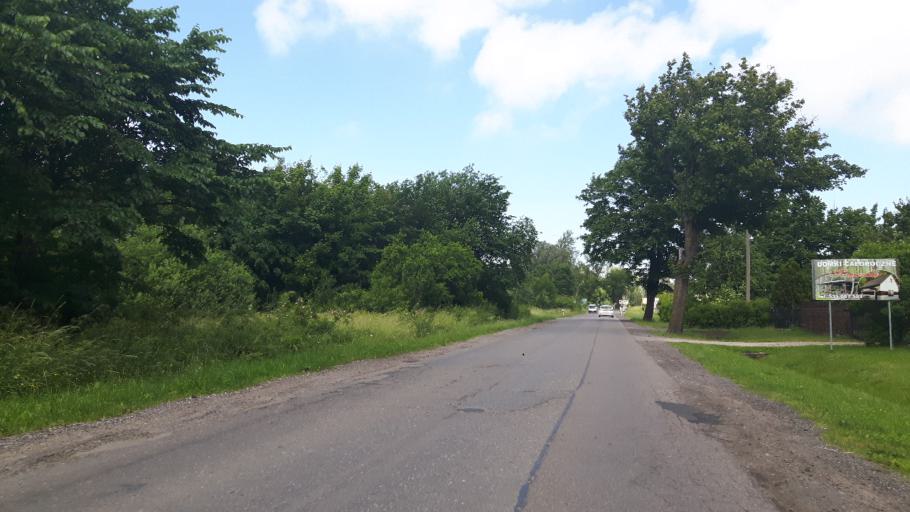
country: PL
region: Pomeranian Voivodeship
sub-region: Powiat slupski
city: Ustka
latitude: 54.5654
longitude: 16.8486
